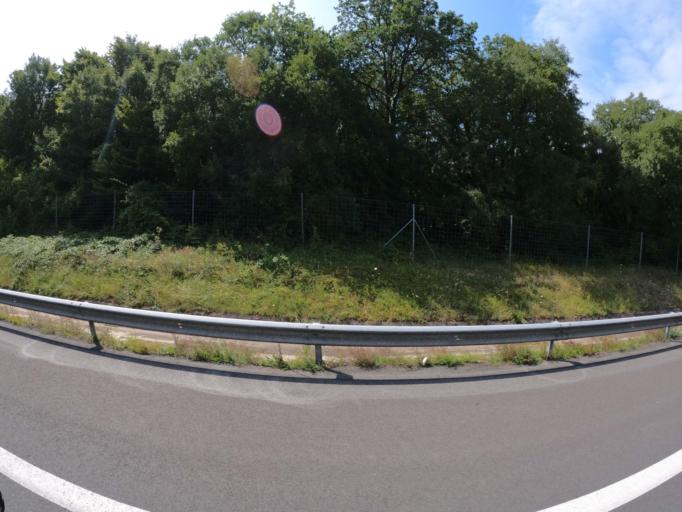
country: FR
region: Poitou-Charentes
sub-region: Departement de la Charente-Maritime
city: Courcon
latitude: 46.2169
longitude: -0.7753
